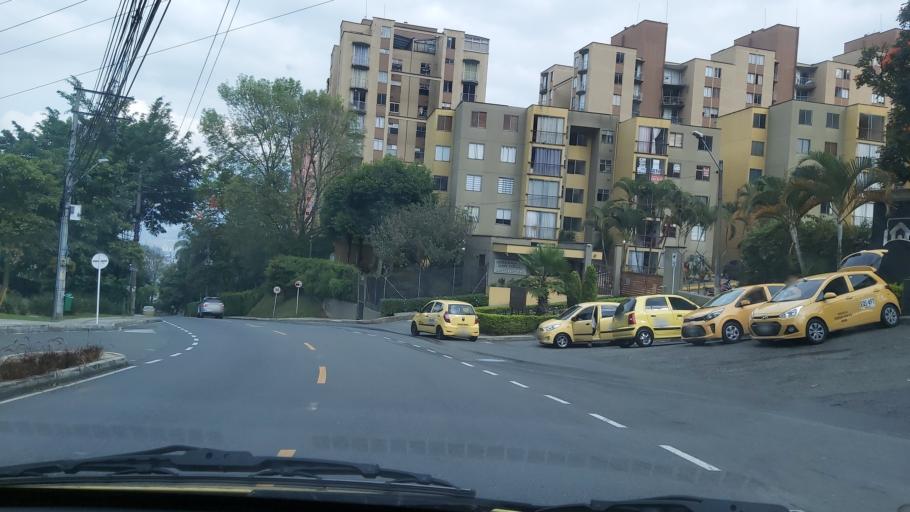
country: CO
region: Antioquia
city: Medellin
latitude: 6.2260
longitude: -75.5611
